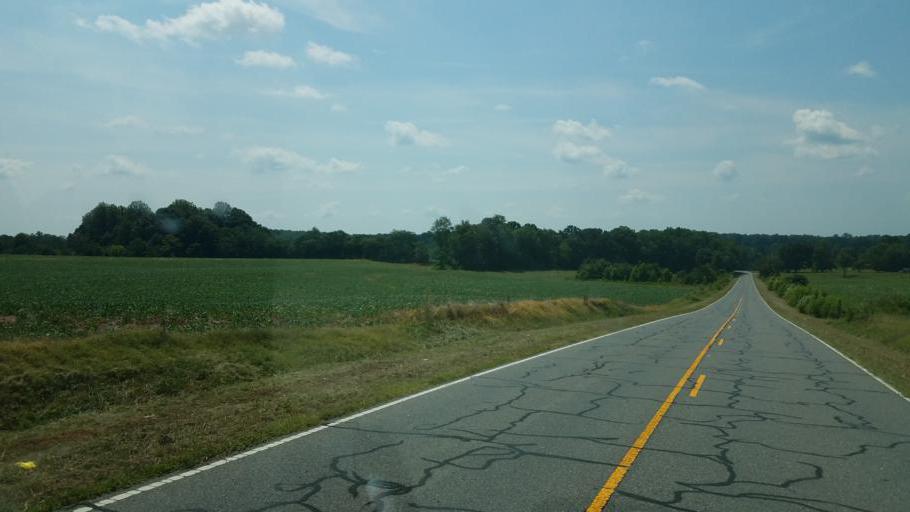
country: US
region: North Carolina
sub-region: Gaston County
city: Cherryville
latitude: 35.4259
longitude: -81.4121
